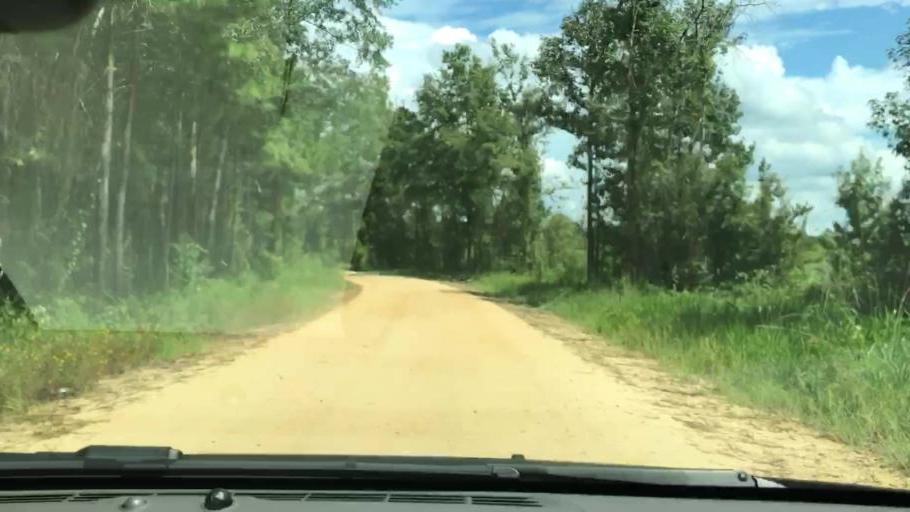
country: US
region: Georgia
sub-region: Quitman County
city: Georgetown
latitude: 32.0365
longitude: -85.0357
